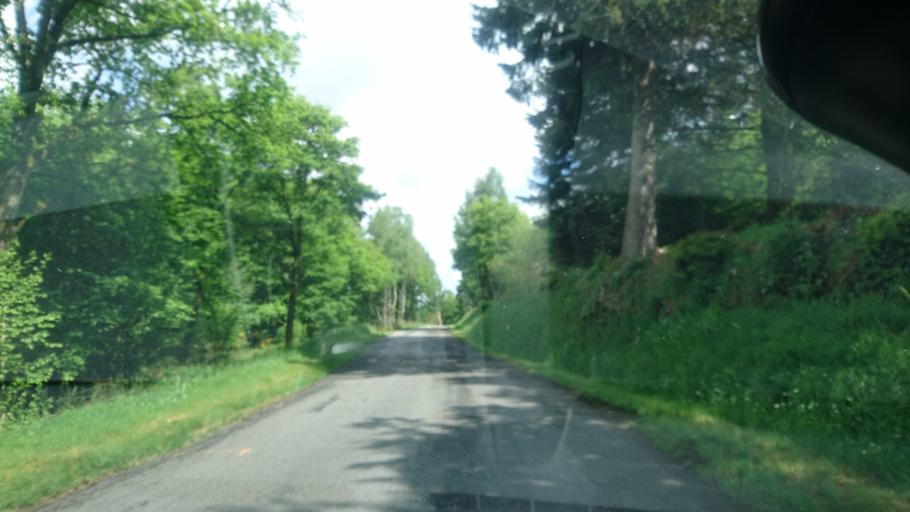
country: FR
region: Limousin
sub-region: Departement de la Haute-Vienne
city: Peyrat-le-Chateau
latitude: 45.7768
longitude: 1.8734
